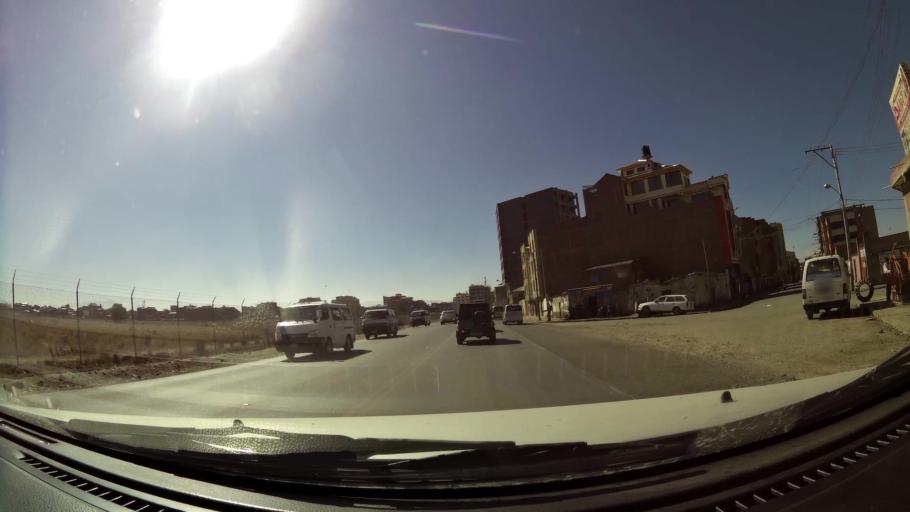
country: BO
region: La Paz
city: La Paz
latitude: -16.5164
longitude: -68.1698
